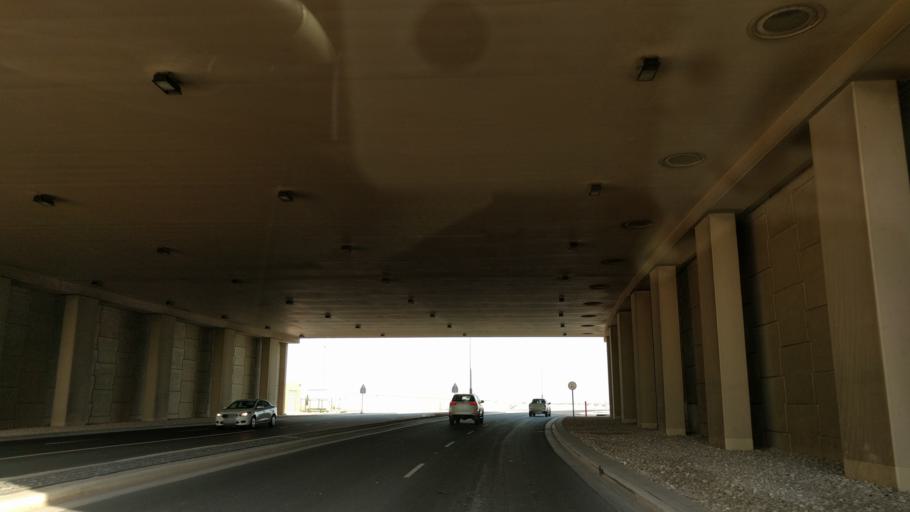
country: AE
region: Abu Dhabi
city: Abu Dhabi
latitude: 24.5493
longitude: 54.4550
